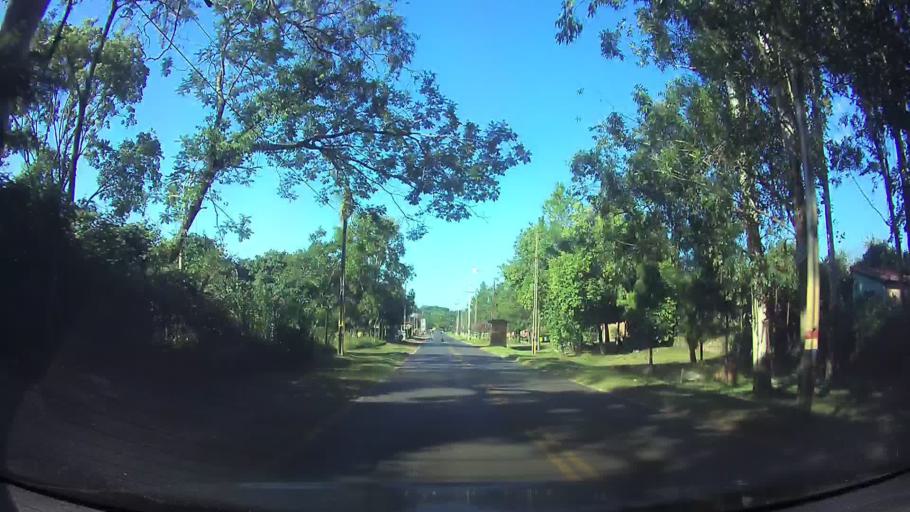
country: PY
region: Cordillera
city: Atyra
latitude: -25.2863
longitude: -57.1782
